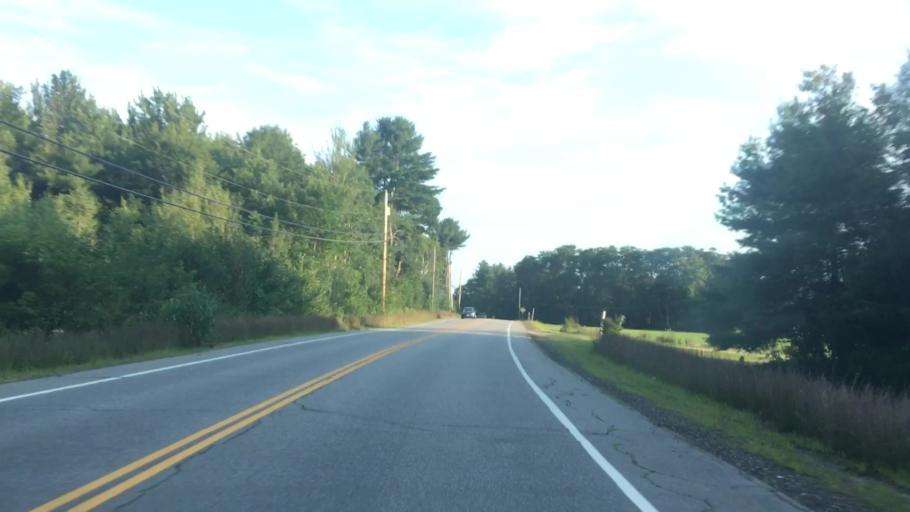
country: US
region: New Hampshire
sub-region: Belknap County
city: Gilmanton
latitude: 43.4375
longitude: -71.4174
